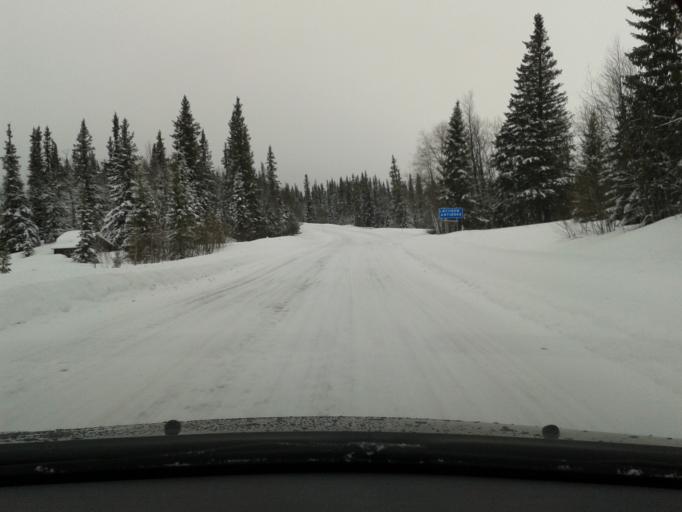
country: SE
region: Vaesterbotten
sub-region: Vilhelmina Kommun
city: Sjoberg
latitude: 65.1429
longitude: 15.8712
